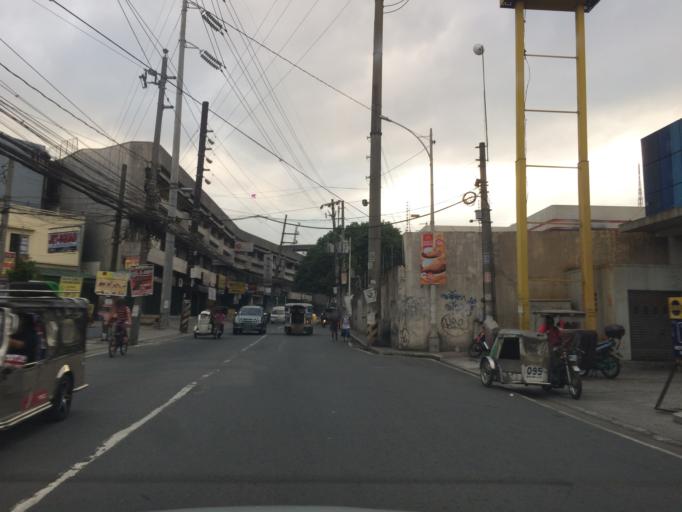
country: PH
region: Calabarzon
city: Bagong Pagasa
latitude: 14.6759
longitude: 121.0443
